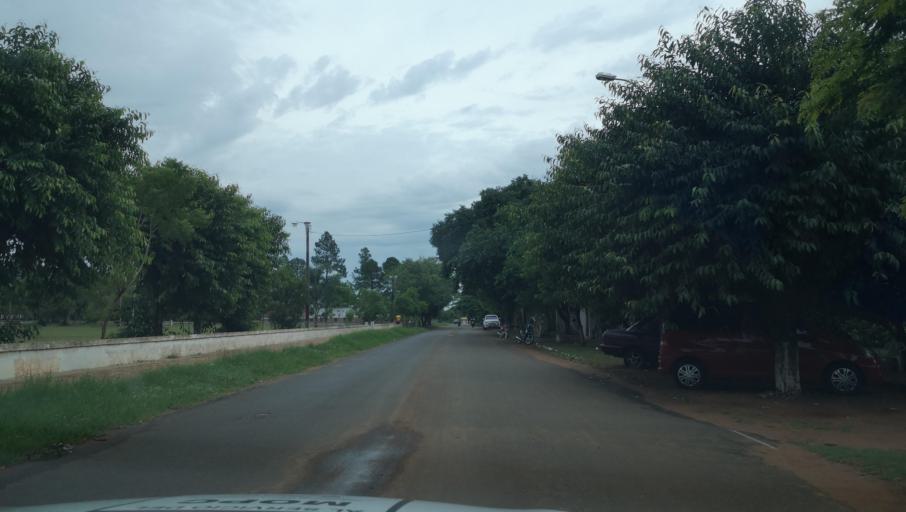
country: PY
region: Misiones
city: Santa Maria
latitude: -26.8888
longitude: -57.0406
